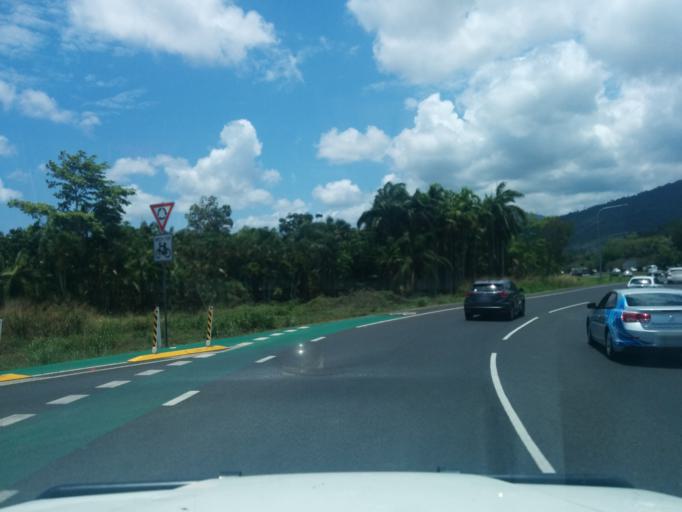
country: AU
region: Queensland
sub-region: Cairns
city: Trinity Beach
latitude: -16.8211
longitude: 145.6936
